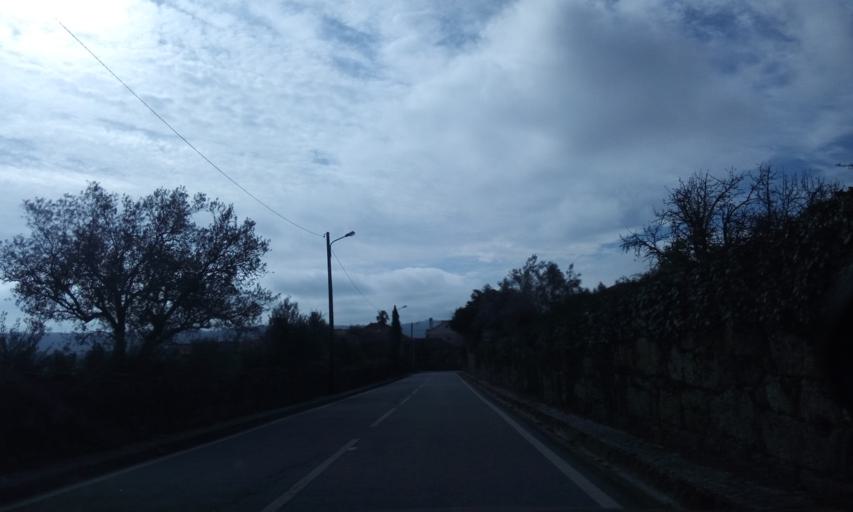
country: PT
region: Guarda
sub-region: Aguiar da Beira
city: Aguiar da Beira
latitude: 40.7343
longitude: -7.5565
